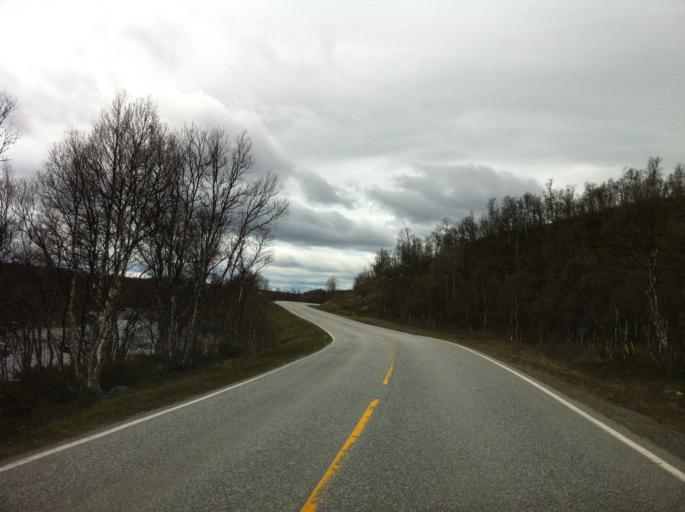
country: NO
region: Sor-Trondelag
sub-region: Roros
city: Roros
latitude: 62.6171
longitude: 11.5804
